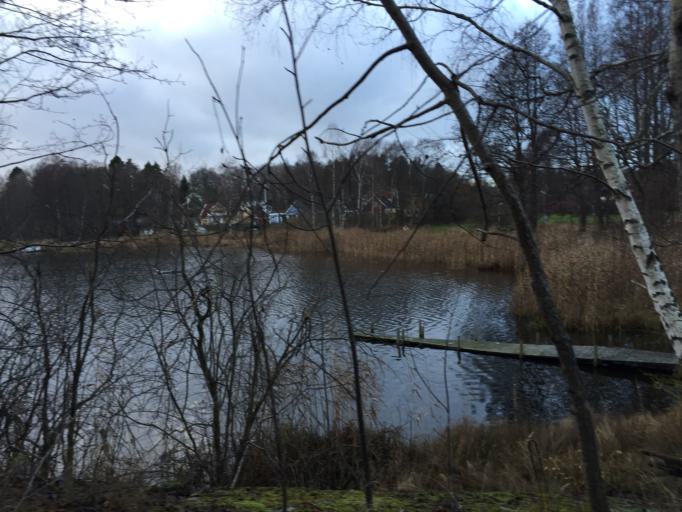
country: SE
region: Stockholm
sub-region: Salems Kommun
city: Ronninge
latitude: 59.1983
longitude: 17.7353
